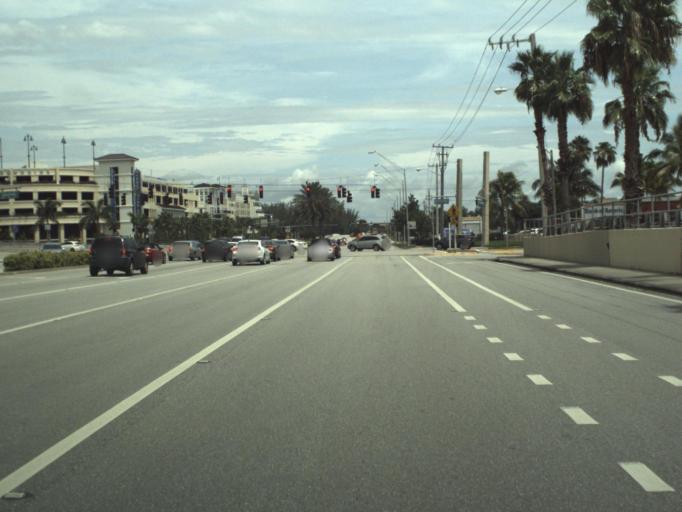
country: US
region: Florida
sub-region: Palm Beach County
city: Jupiter
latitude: 26.9332
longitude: -80.0803
